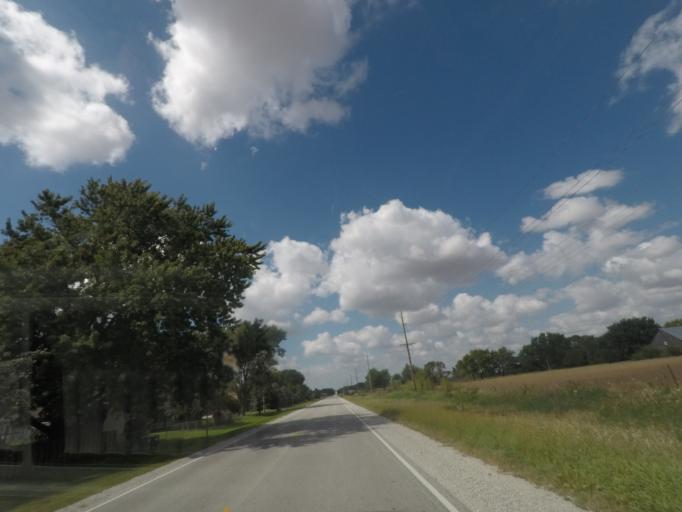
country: US
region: Iowa
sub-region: Story County
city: Nevada
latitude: 42.0225
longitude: -93.3204
